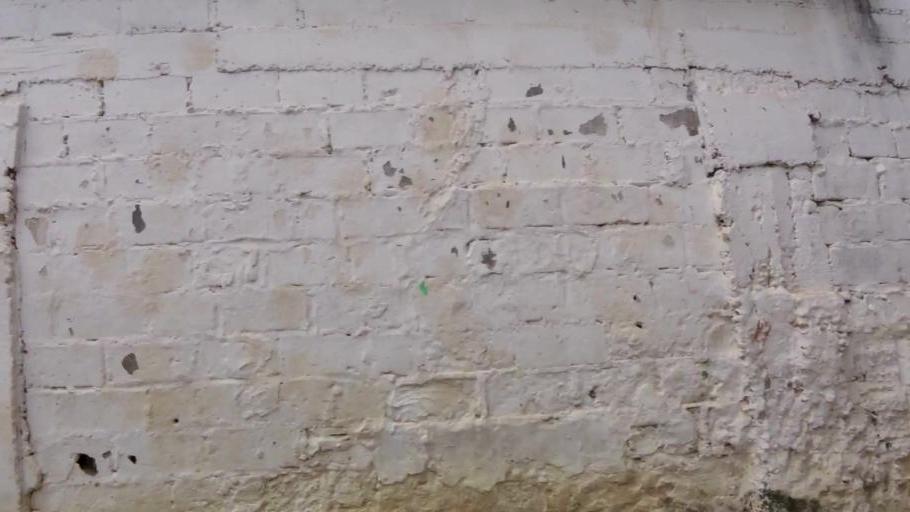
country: CO
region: Bolivar
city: Cartagena
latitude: 10.3714
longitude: -75.5074
